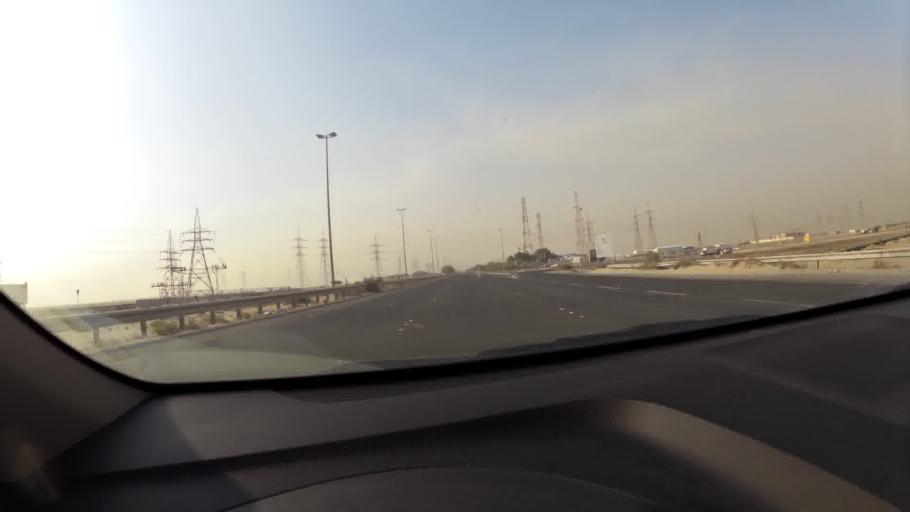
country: SA
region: Eastern Province
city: Al Khafji
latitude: 28.7369
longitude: 48.2847
